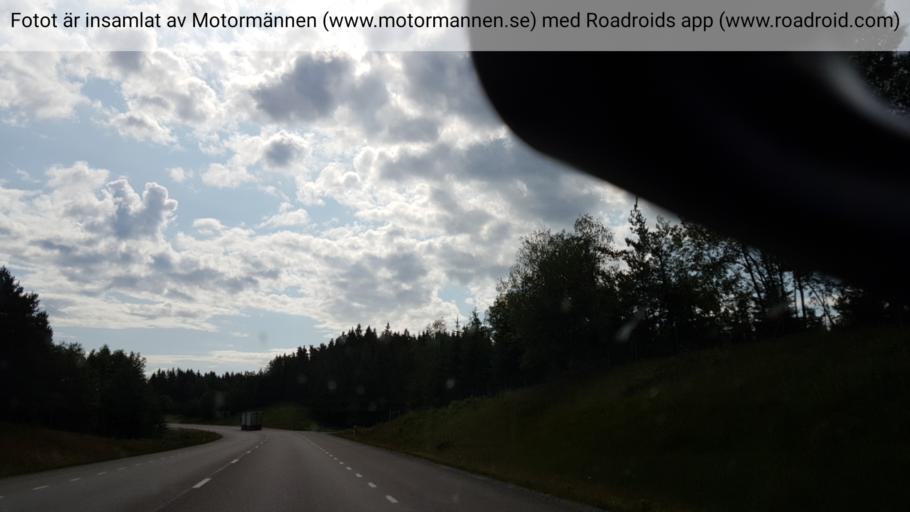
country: SE
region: Vaestra Goetaland
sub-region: Vanersborgs Kommun
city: Vargon
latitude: 58.3032
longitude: 12.5298
